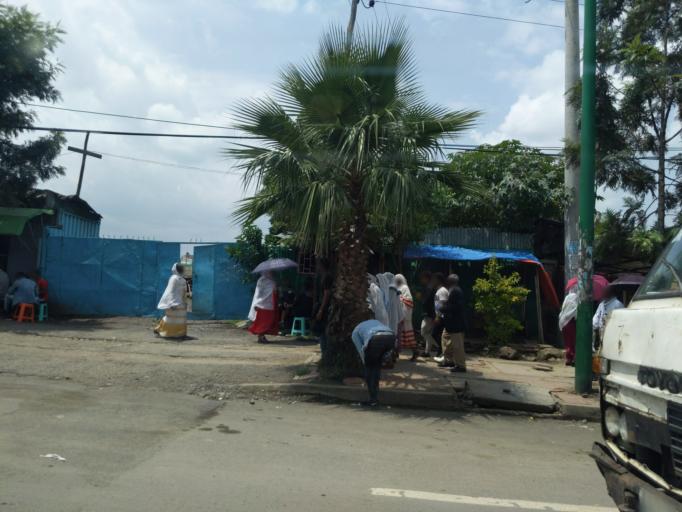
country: ET
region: Adis Abeba
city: Addis Ababa
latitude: 8.9503
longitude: 38.7639
